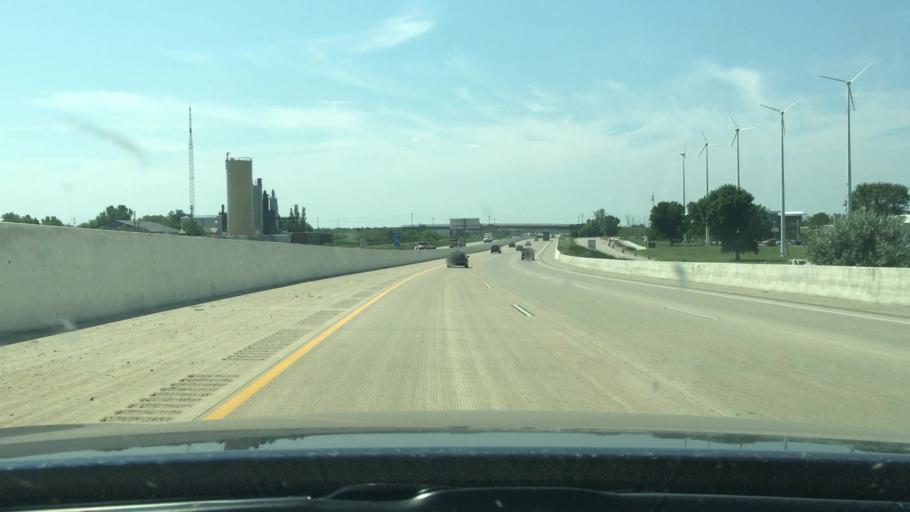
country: US
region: Wisconsin
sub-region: Winnebago County
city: Neenah
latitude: 44.1479
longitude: -88.4877
